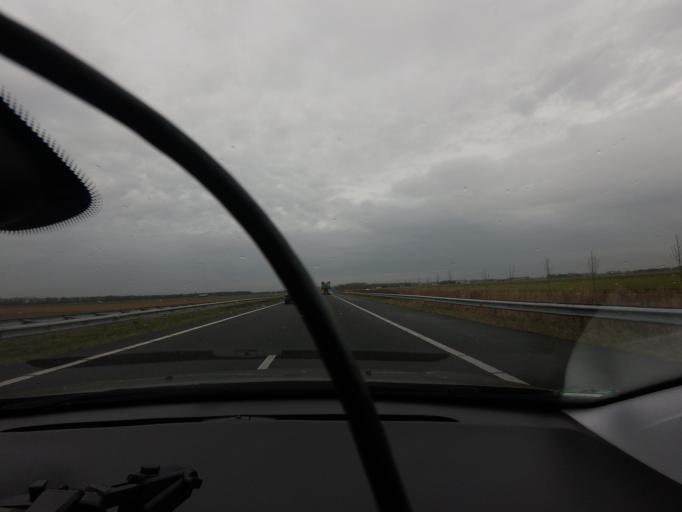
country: NL
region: North Holland
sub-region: Gemeente Medemblik
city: Opperdoes
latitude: 52.7923
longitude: 5.0212
